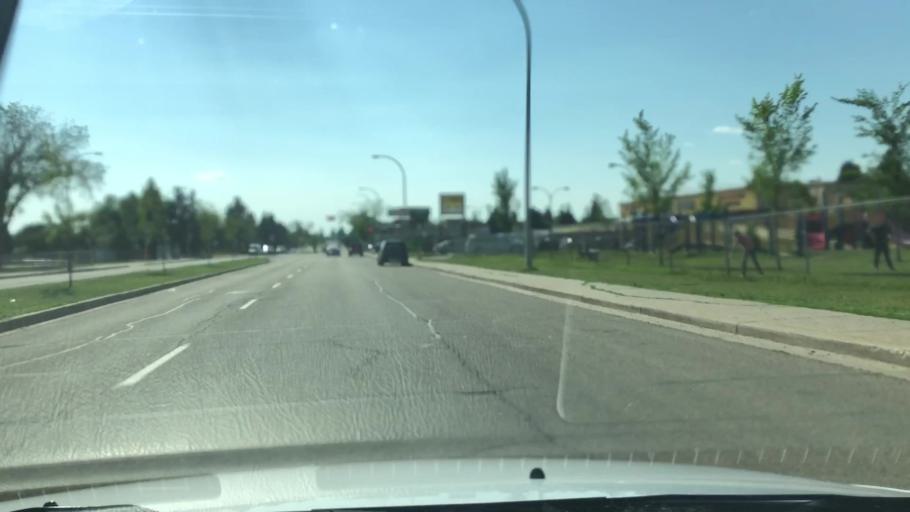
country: CA
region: Alberta
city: Edmonton
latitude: 53.6070
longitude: -113.4566
